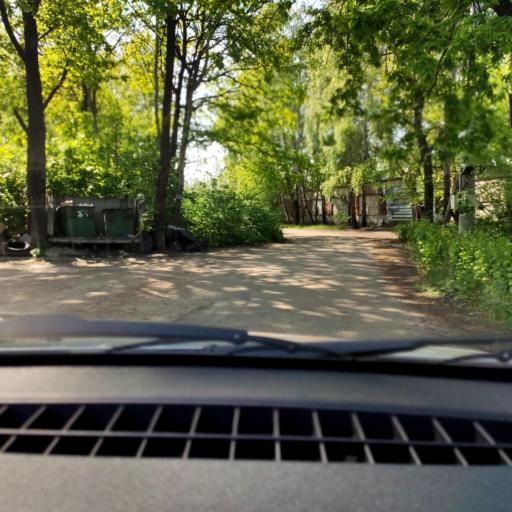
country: RU
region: Voronezj
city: Podgornoye
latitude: 51.7439
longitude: 39.1725
